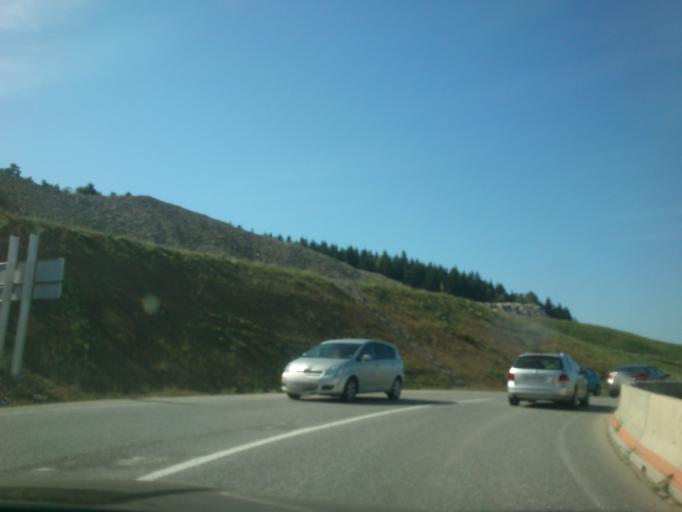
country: AT
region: Upper Austria
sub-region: Politischer Bezirk Urfahr-Umgebung
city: Alberndorf in der Riedmark
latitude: 48.4185
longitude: 14.4909
